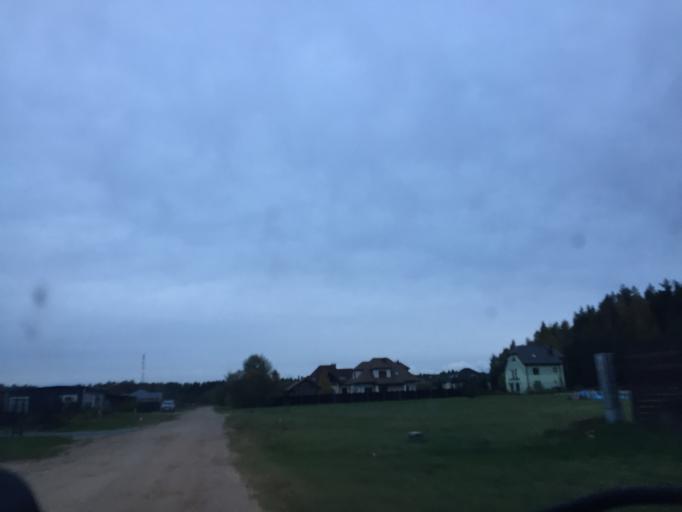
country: LV
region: Adazi
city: Adazi
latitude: 57.0852
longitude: 24.3772
